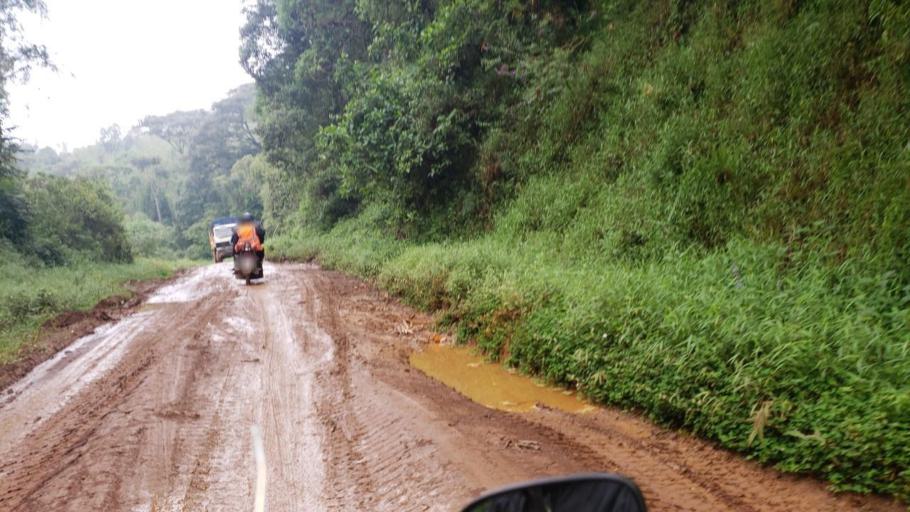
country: CD
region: South Kivu
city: Kabare
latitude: -2.2633
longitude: 28.6603
